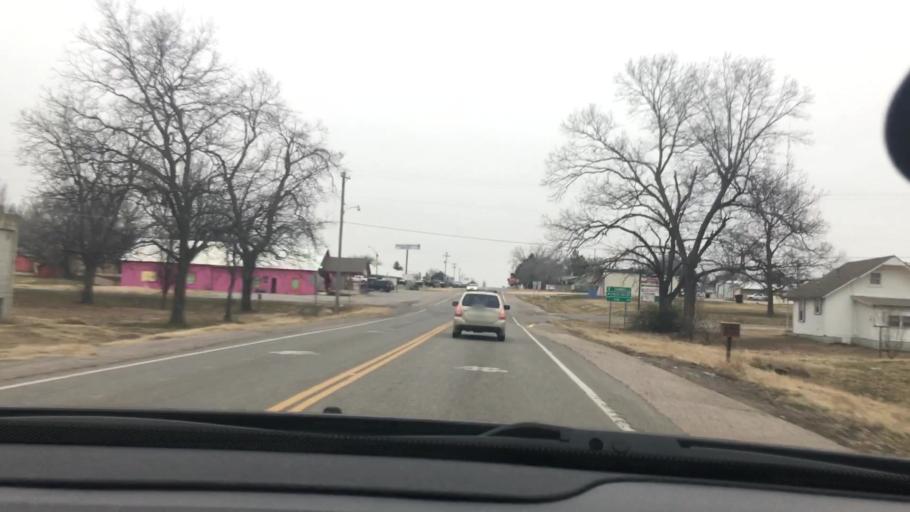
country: US
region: Oklahoma
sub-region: Garvin County
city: Stratford
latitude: 34.7948
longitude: -96.9674
